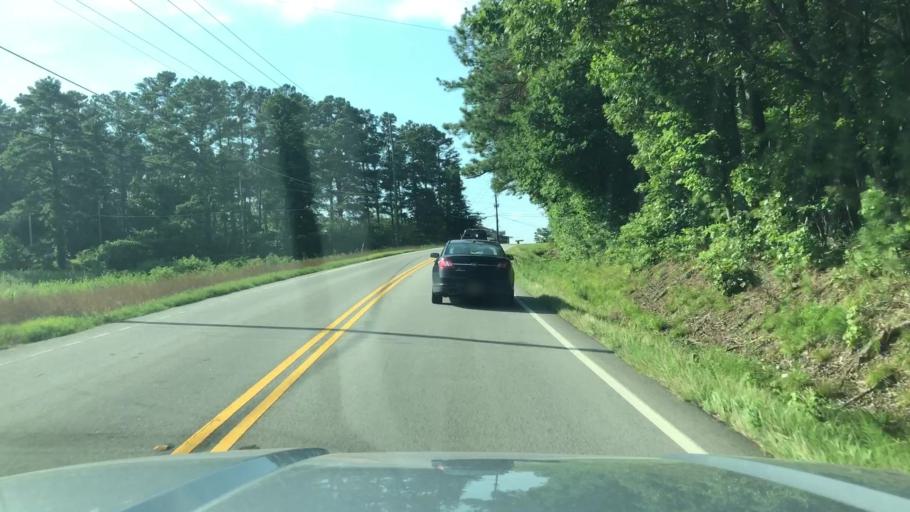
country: US
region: Georgia
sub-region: Paulding County
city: Dallas
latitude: 33.9867
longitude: -84.8711
